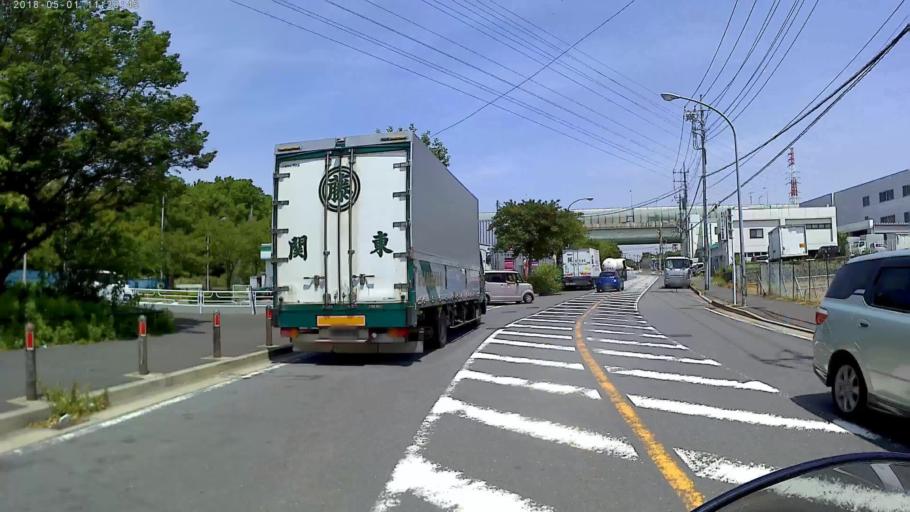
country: JP
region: Kanagawa
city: Minami-rinkan
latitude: 35.5023
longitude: 139.4867
